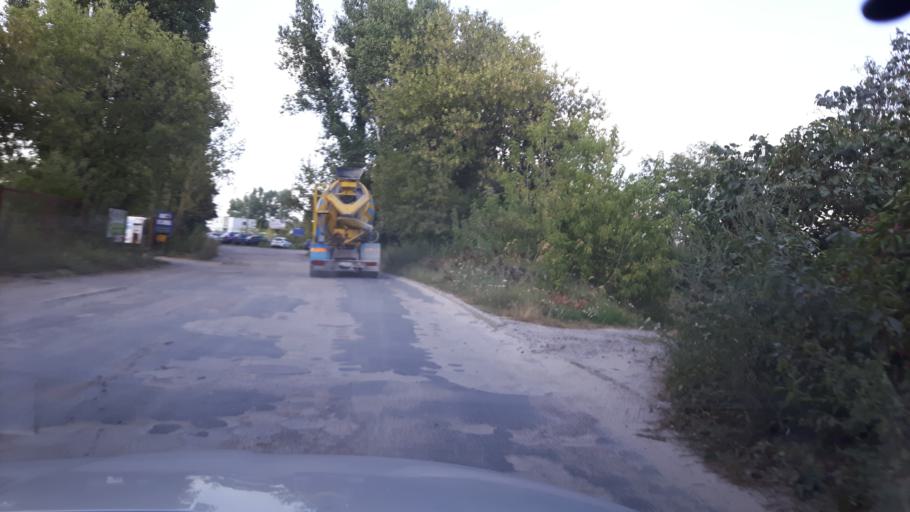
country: PL
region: Masovian Voivodeship
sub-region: Warszawa
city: Praga Polnoc
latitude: 52.2698
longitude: 21.0240
